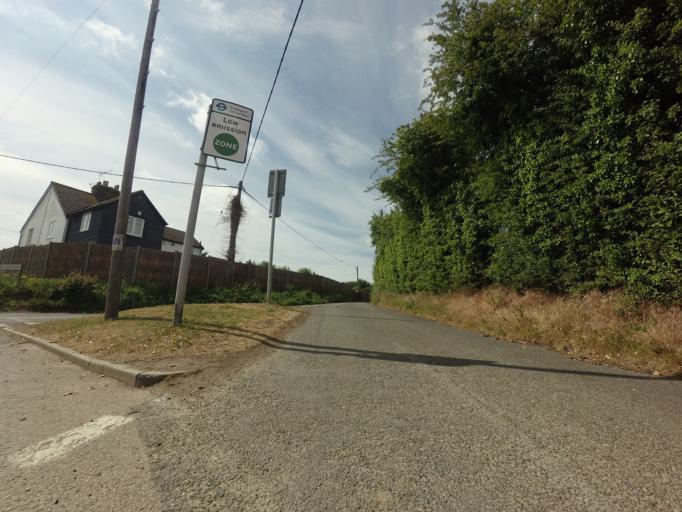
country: GB
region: England
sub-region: Greater London
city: Orpington
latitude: 51.3739
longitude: 0.1382
